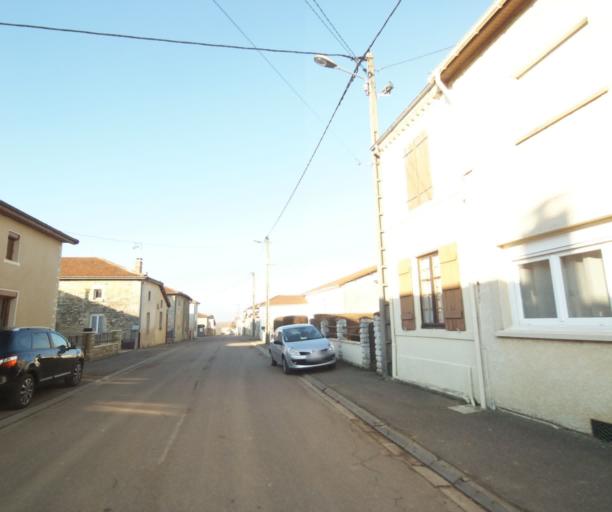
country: FR
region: Champagne-Ardenne
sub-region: Departement de la Haute-Marne
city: Bienville
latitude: 48.5834
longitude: 5.0873
